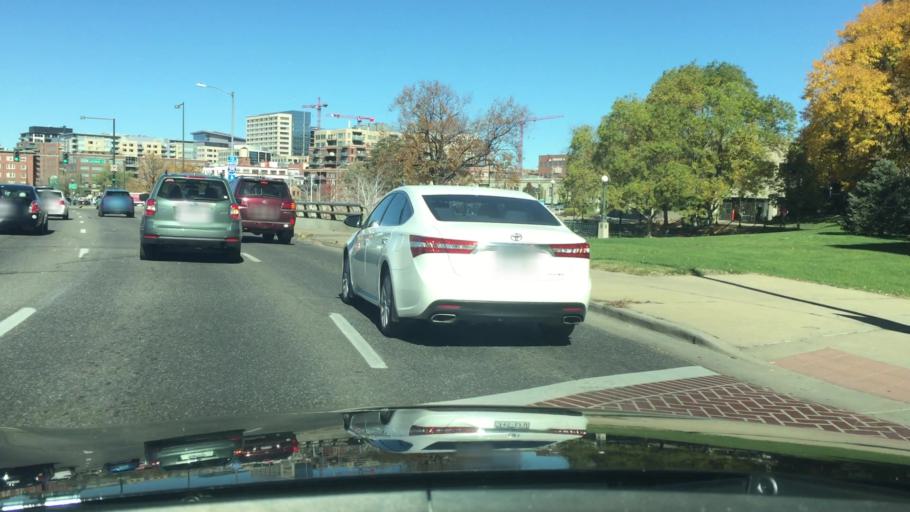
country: US
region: Colorado
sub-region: Denver County
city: Denver
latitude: 39.7458
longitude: -105.0002
